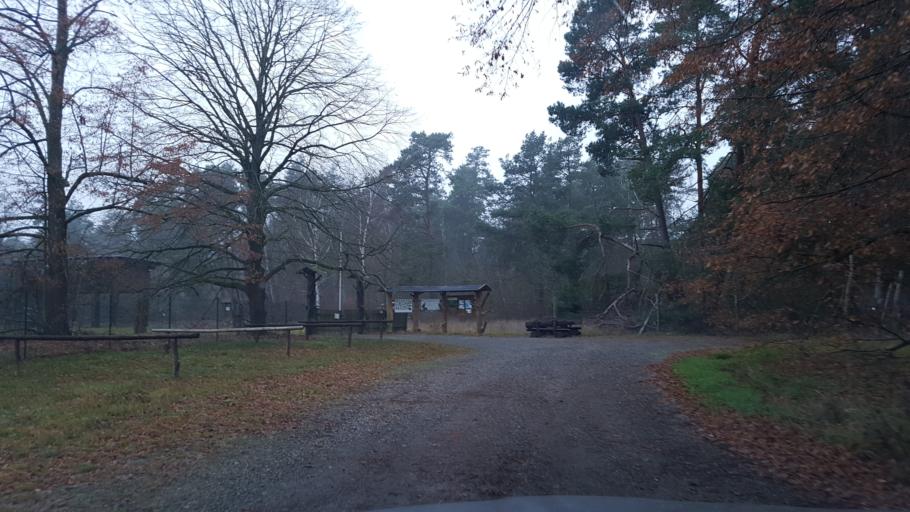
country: DE
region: Brandenburg
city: Ruckersdorf
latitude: 51.5441
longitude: 13.5752
